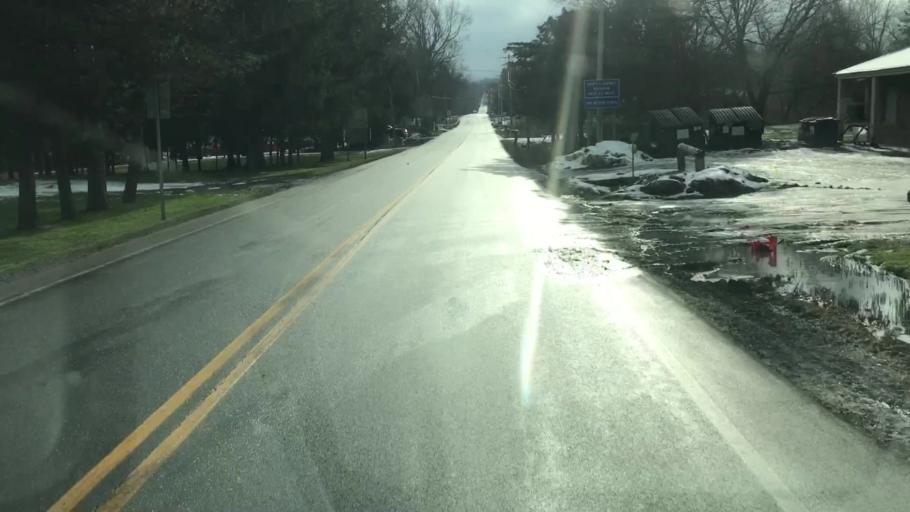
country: US
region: New York
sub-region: Onondaga County
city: Skaneateles
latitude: 42.8650
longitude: -76.4029
